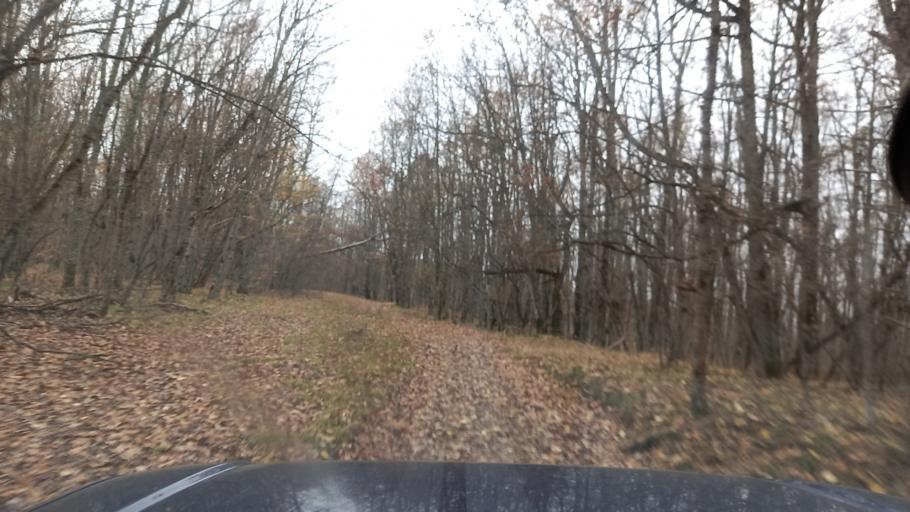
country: RU
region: Krasnodarskiy
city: Goryachiy Klyuch
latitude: 44.5049
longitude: 39.2855
